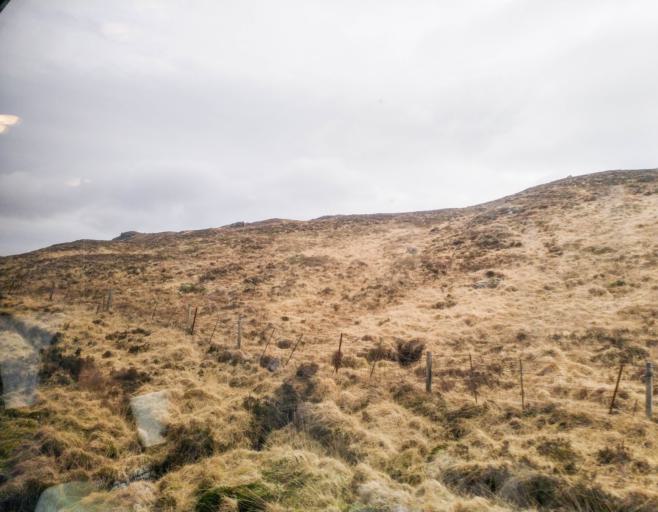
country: GB
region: Scotland
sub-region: Highland
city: Spean Bridge
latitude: 56.5885
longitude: -4.6559
